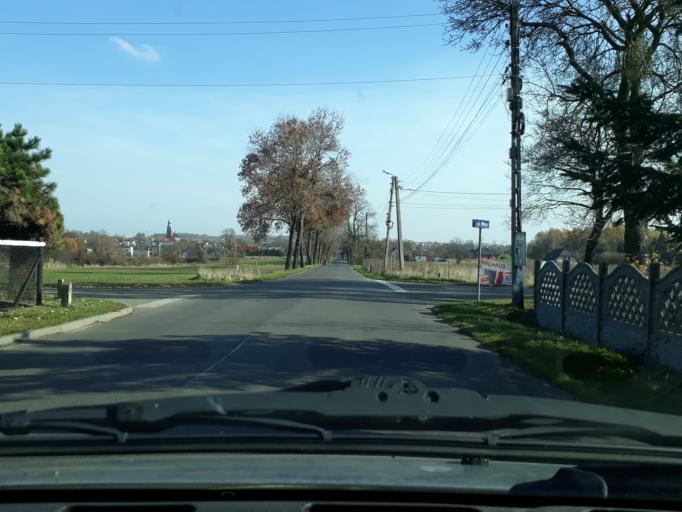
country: PL
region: Silesian Voivodeship
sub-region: Powiat tarnogorski
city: Tarnowskie Gory
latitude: 50.4249
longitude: 18.8524
